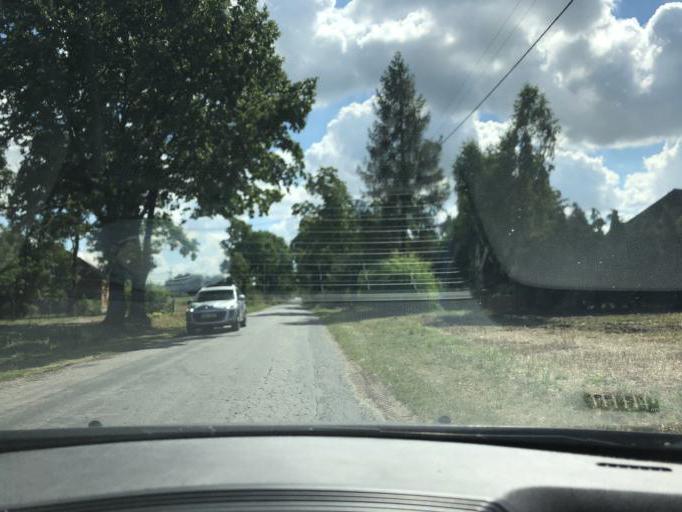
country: PL
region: Lodz Voivodeship
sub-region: Powiat wieruszowski
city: Czastary
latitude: 51.2337
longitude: 18.3496
